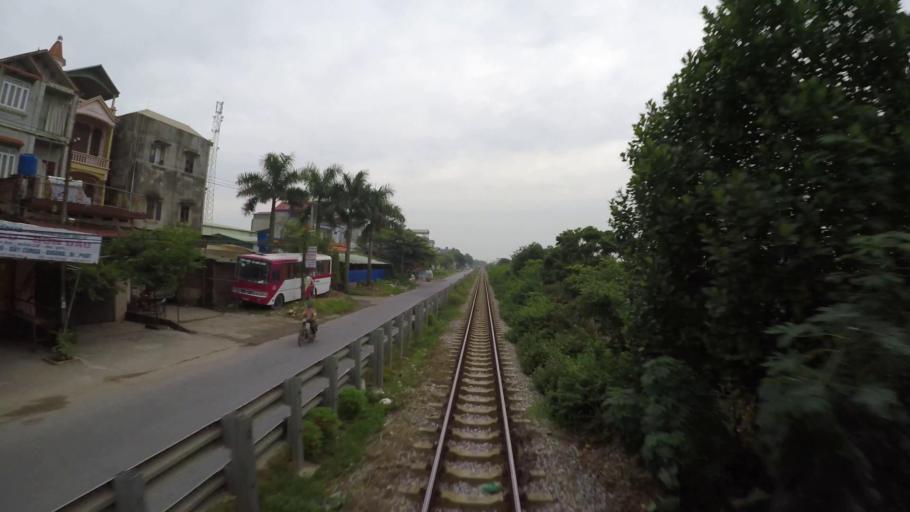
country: VN
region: Hung Yen
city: Ban Yen Nhan
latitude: 20.9667
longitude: 106.1086
